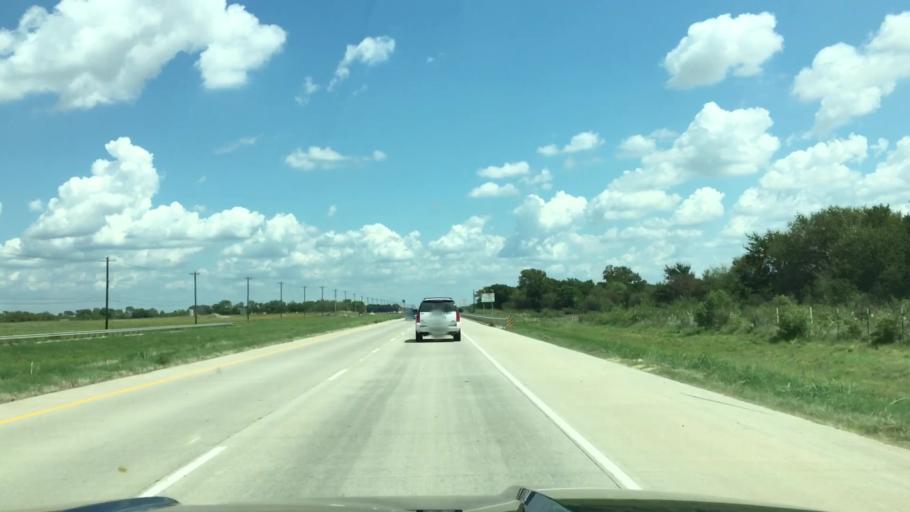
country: US
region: Texas
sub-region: Tarrant County
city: Haslet
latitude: 33.0354
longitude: -97.3677
